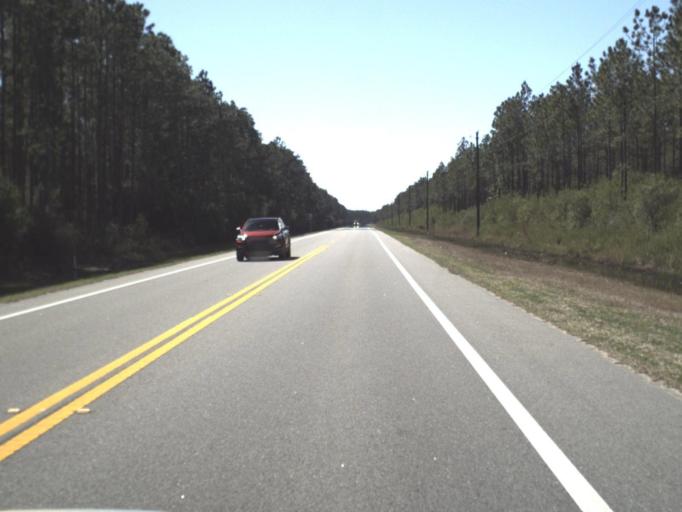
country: US
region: Florida
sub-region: Bay County
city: Laguna Beach
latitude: 30.3080
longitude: -85.8196
